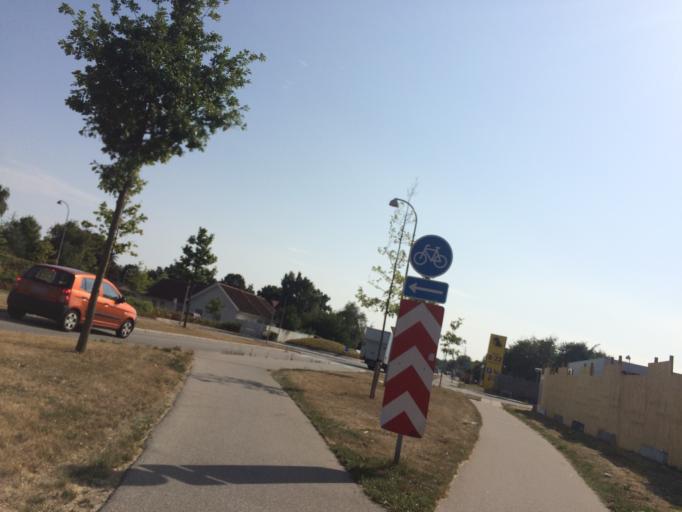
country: DK
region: Capital Region
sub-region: Ishoj Kommune
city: Ishoj
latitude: 55.6054
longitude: 12.3547
